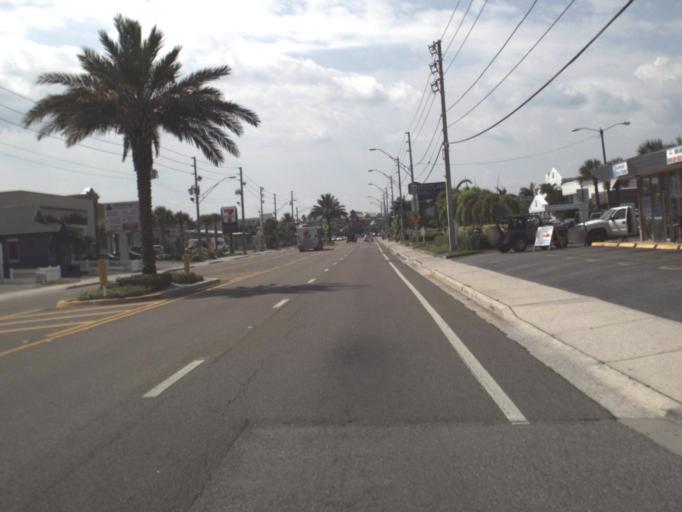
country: US
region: Florida
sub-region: Pinellas County
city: Saint Pete Beach
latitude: 27.7352
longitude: -82.7469
